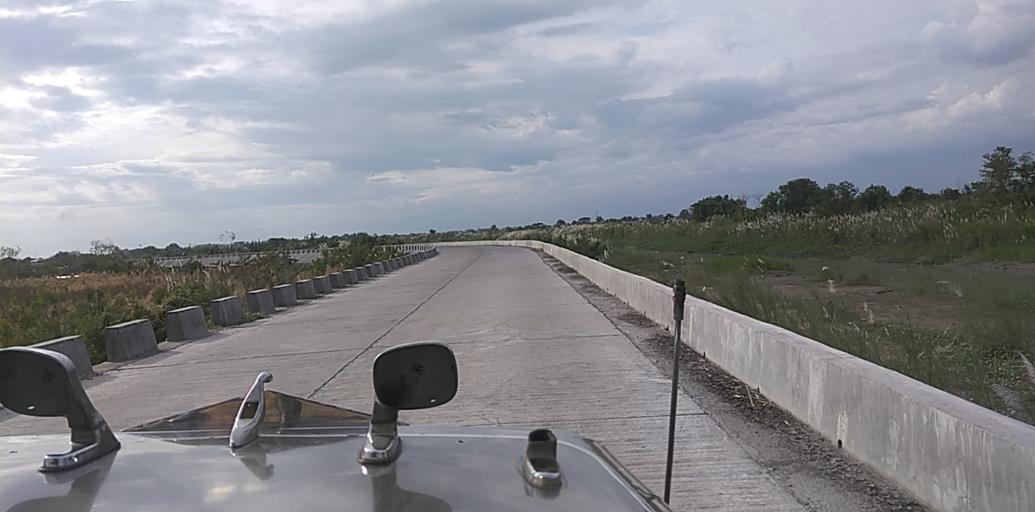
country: PH
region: Central Luzon
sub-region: Province of Pampanga
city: Minalin
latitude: 14.9674
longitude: 120.6663
